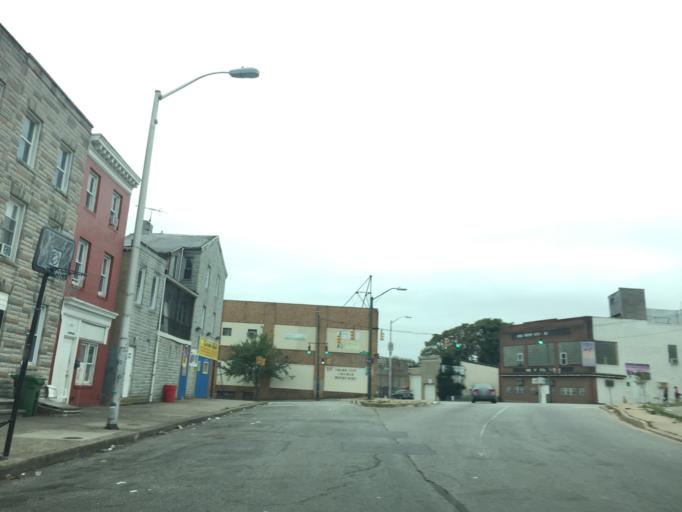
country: US
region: Maryland
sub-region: City of Baltimore
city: Baltimore
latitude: 39.2861
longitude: -76.6478
